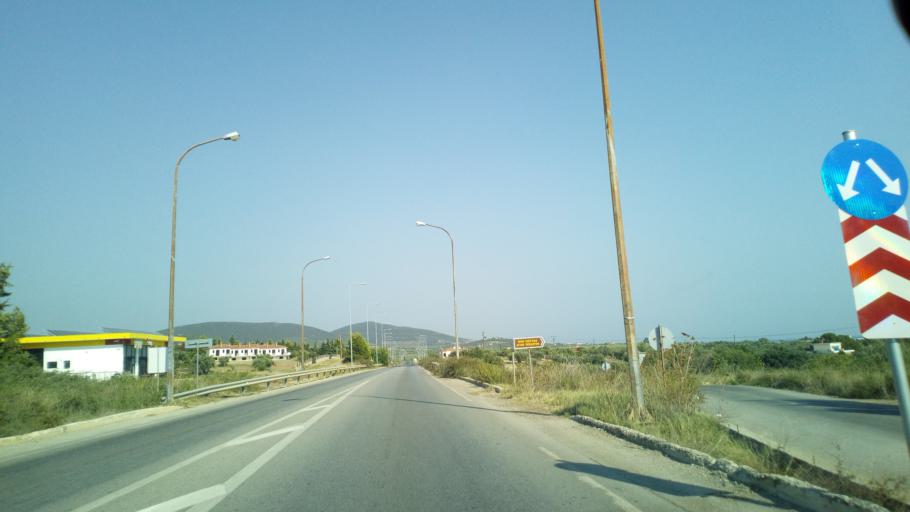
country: GR
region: Central Macedonia
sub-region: Nomos Chalkidikis
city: Kalyves Polygyrou
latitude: 40.2791
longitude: 23.4316
